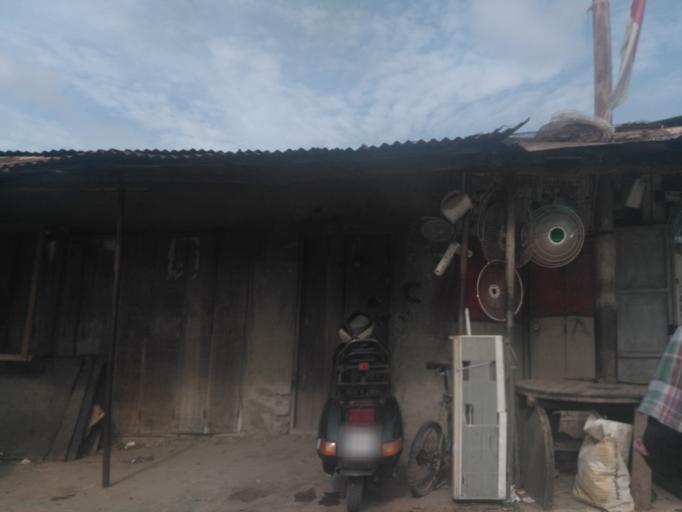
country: TZ
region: Zanzibar Urban/West
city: Zanzibar
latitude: -6.1651
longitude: 39.2110
